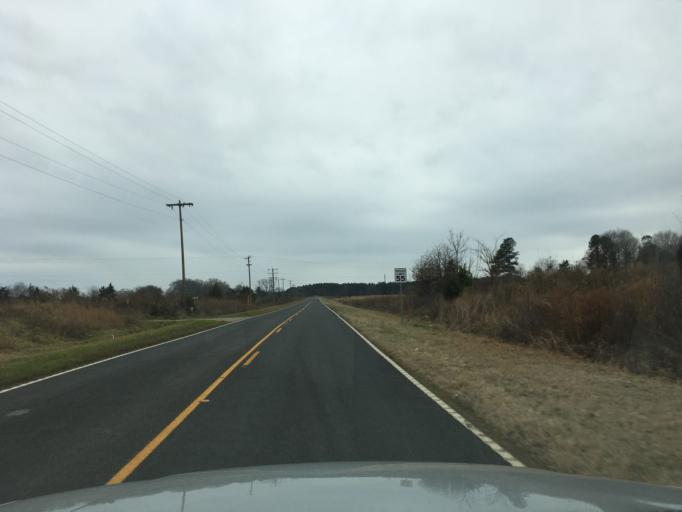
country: US
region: South Carolina
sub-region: Greenwood County
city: Greenwood
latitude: 34.1254
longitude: -82.1606
